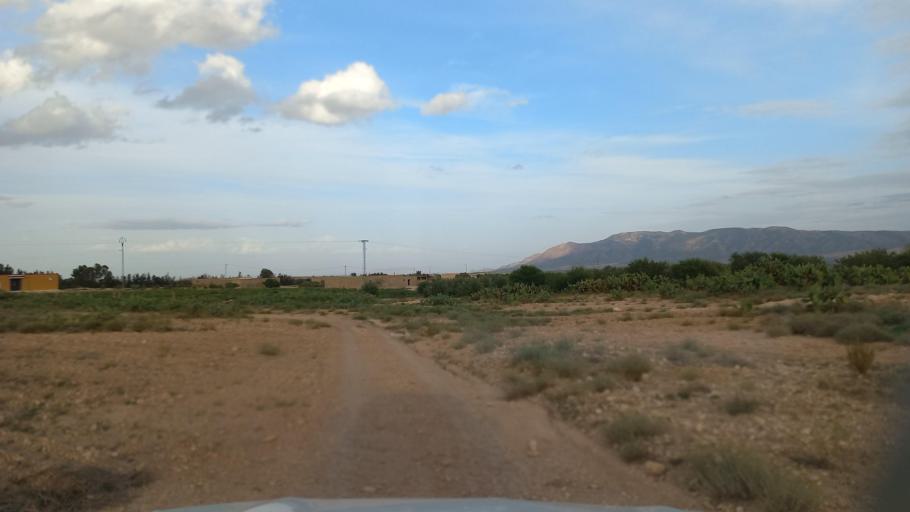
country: TN
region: Al Qasrayn
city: Sbiba
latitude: 35.4393
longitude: 9.0904
